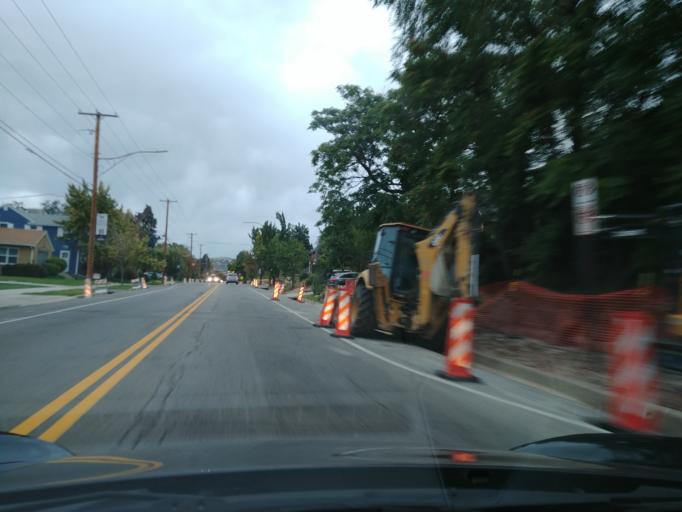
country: US
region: Utah
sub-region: Salt Lake County
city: Willard
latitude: 40.7381
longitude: -111.8538
